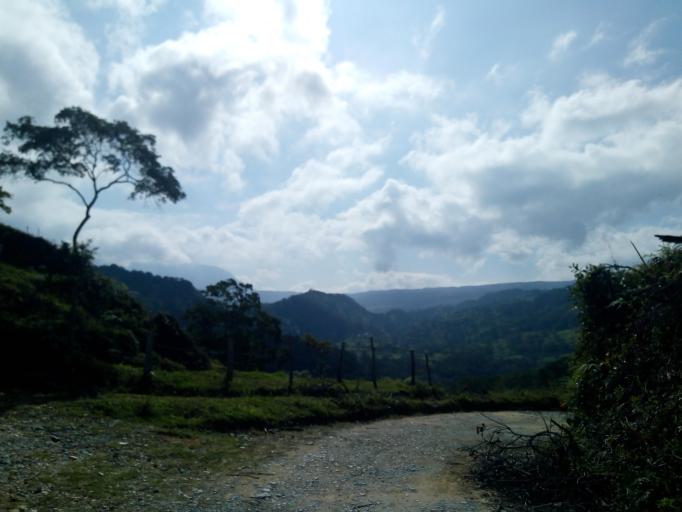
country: CO
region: Boyaca
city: Moniquira
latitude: 5.8833
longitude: -73.5094
